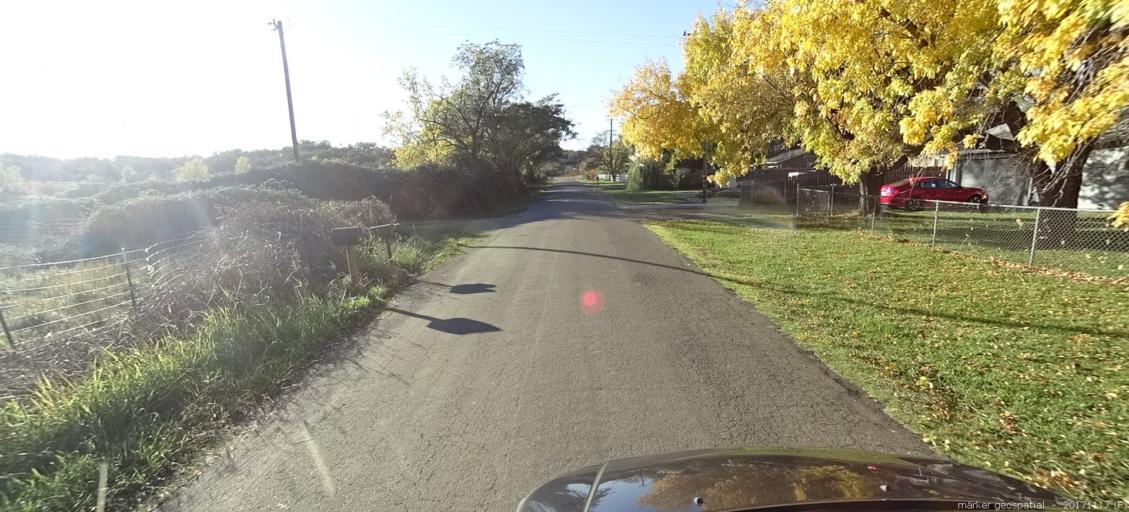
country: US
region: California
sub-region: Shasta County
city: Cottonwood
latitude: 40.4162
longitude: -122.2462
